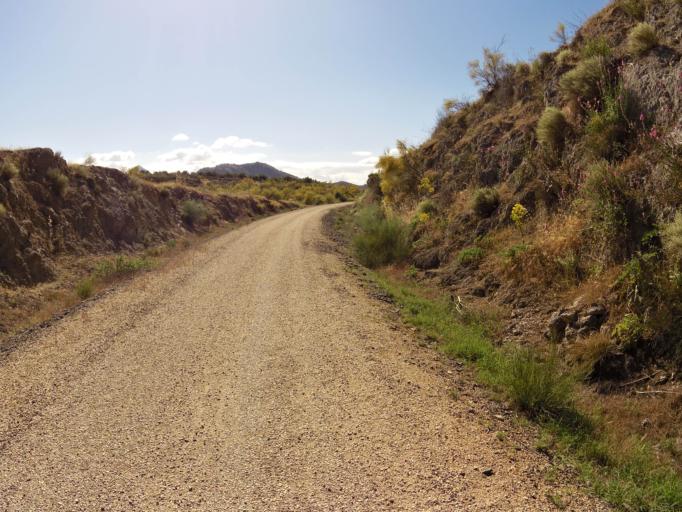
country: ES
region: Andalusia
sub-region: Provincia de Jaen
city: Alcaudete
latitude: 37.6053
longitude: -4.1543
